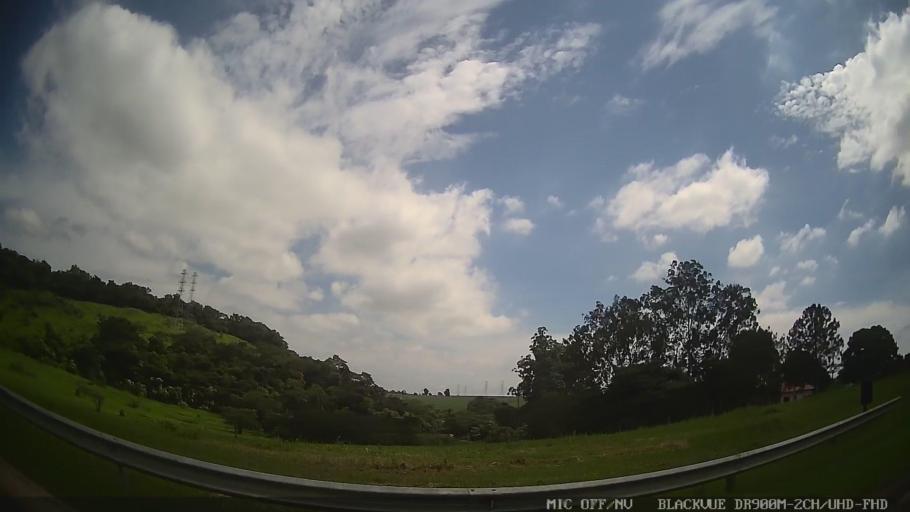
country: BR
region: Sao Paulo
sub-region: Tiete
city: Tiete
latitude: -23.1092
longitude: -47.7504
